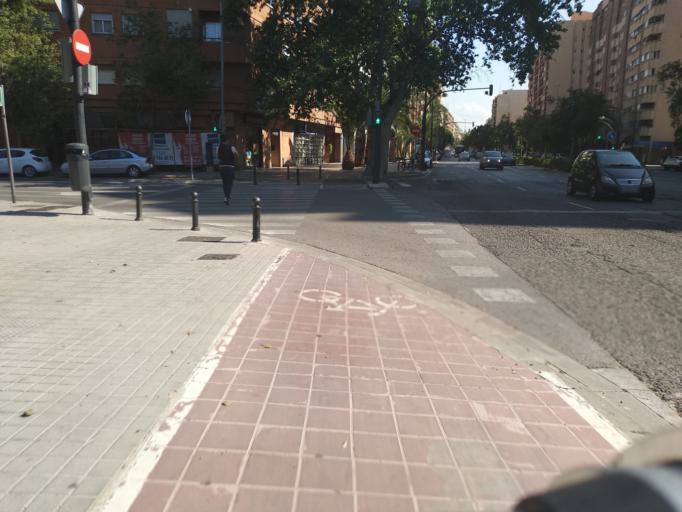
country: ES
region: Valencia
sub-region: Provincia de Valencia
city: Alboraya
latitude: 39.4785
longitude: -0.3511
